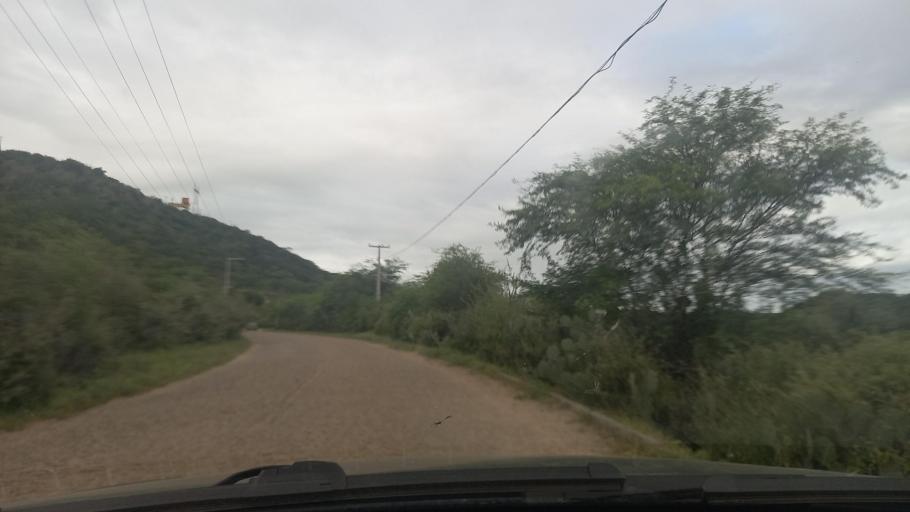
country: BR
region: Sergipe
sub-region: Caninde De Sao Francisco
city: Caninde de Sao Francisco
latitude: -9.6280
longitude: -37.8051
